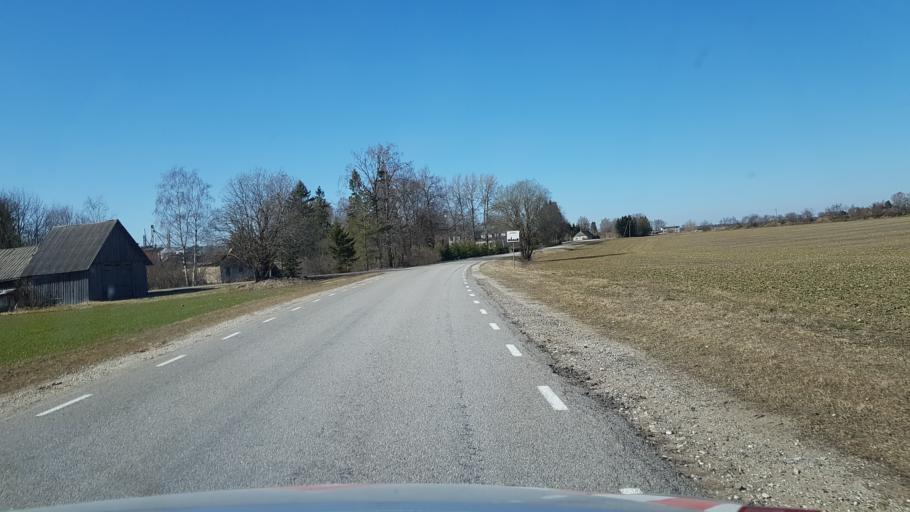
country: EE
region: Laeaene-Virumaa
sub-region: Vaeike-Maarja vald
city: Vaike-Maarja
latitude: 59.1076
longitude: 26.3805
